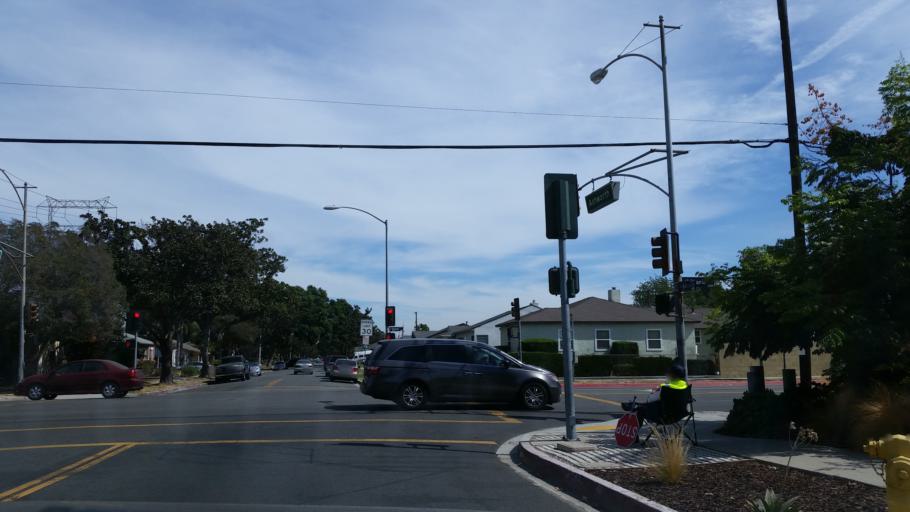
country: US
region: California
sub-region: Los Angeles County
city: Lakewood
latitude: 33.8678
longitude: -118.1342
